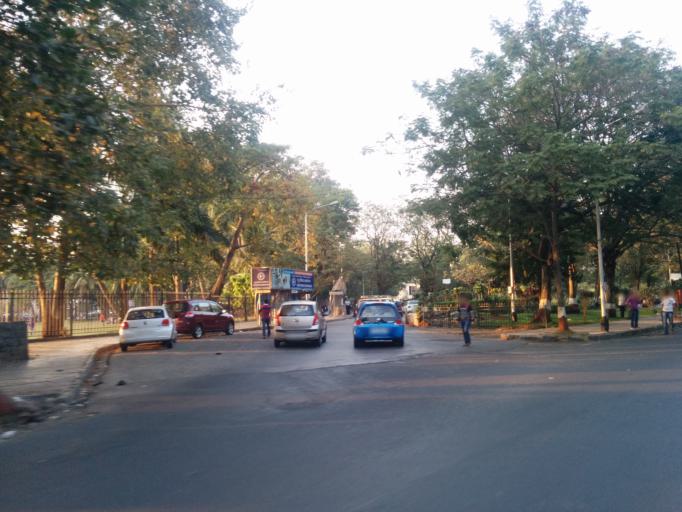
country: IN
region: Maharashtra
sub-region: Raigarh
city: Uran
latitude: 18.9319
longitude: 72.8299
